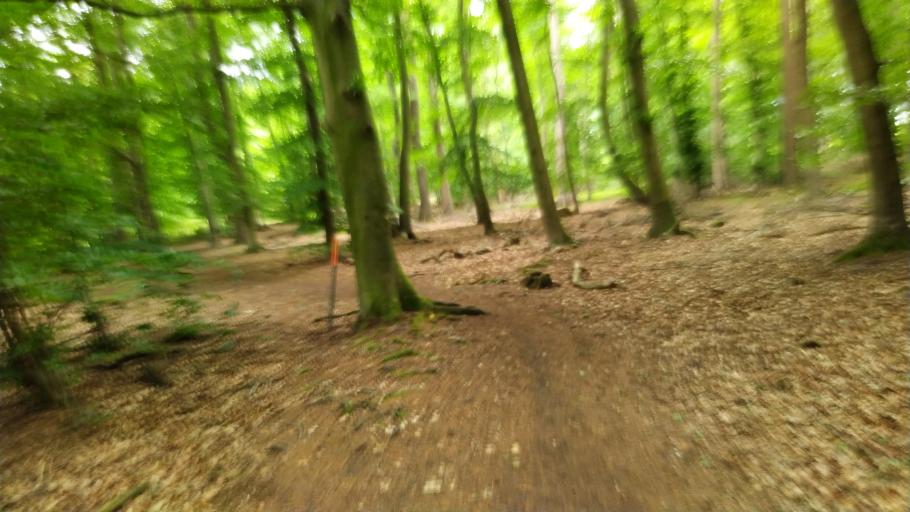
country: DE
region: Lower Saxony
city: Deinstedt
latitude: 53.4408
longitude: 9.1912
